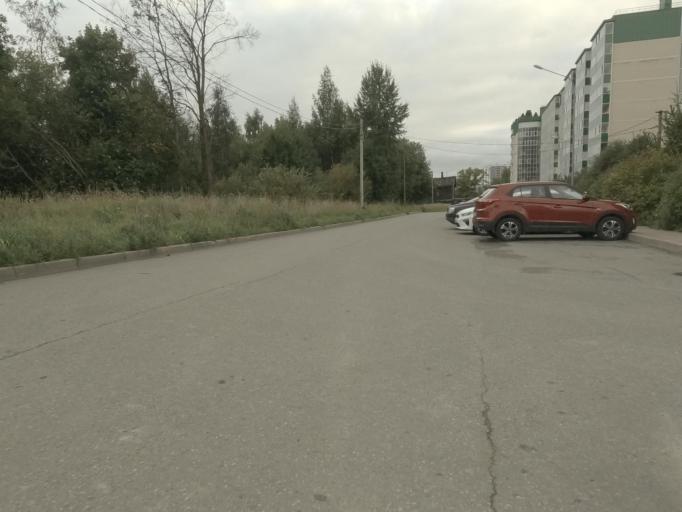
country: RU
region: St.-Petersburg
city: Krasnogvargeisky
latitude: 59.9647
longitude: 30.4952
